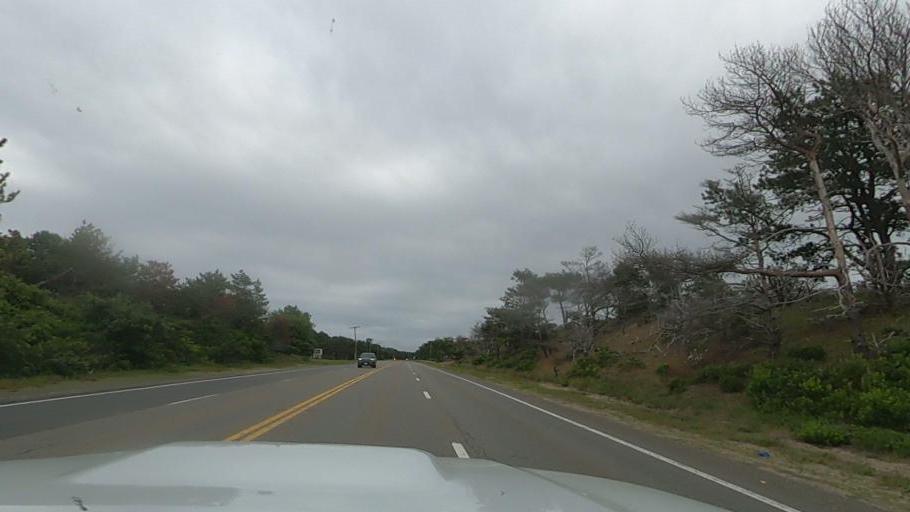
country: US
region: Massachusetts
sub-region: Barnstable County
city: Provincetown
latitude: 42.0493
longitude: -70.1117
